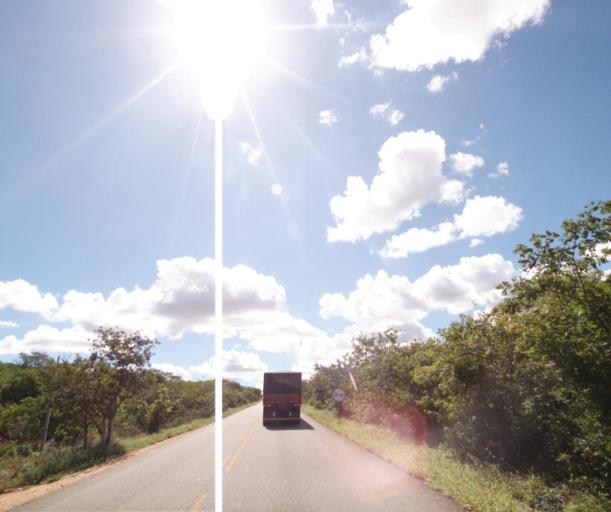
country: BR
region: Bahia
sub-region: Caetite
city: Caetite
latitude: -14.1719
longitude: -42.2078
